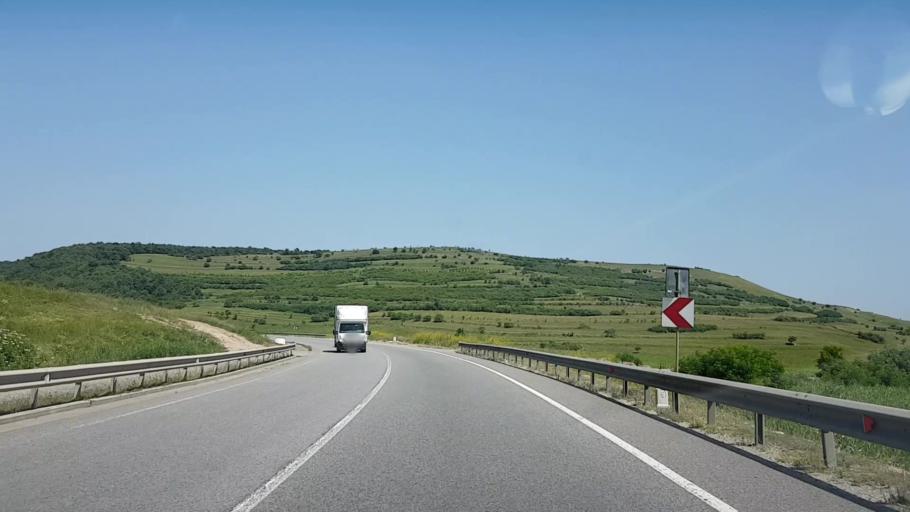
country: RO
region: Cluj
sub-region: Comuna Feleacu
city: Gheorghieni
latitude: 46.7325
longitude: 23.7031
